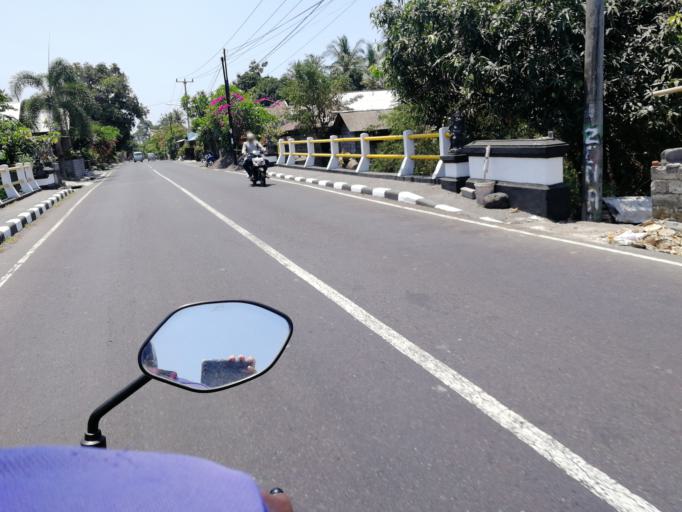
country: ID
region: Bali
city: Banjar Trunyan
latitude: -8.1422
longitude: 115.3915
